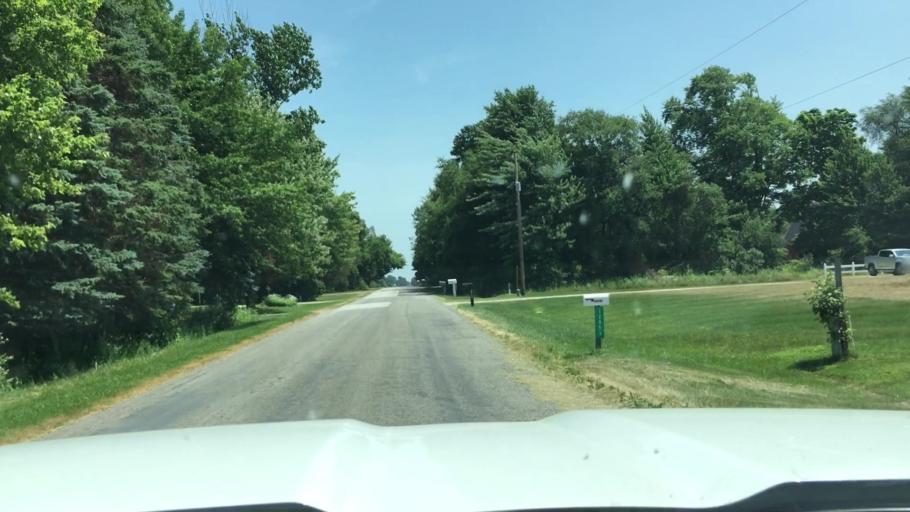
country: US
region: Michigan
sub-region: Saginaw County
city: Chesaning
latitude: 43.2155
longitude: -84.1664
